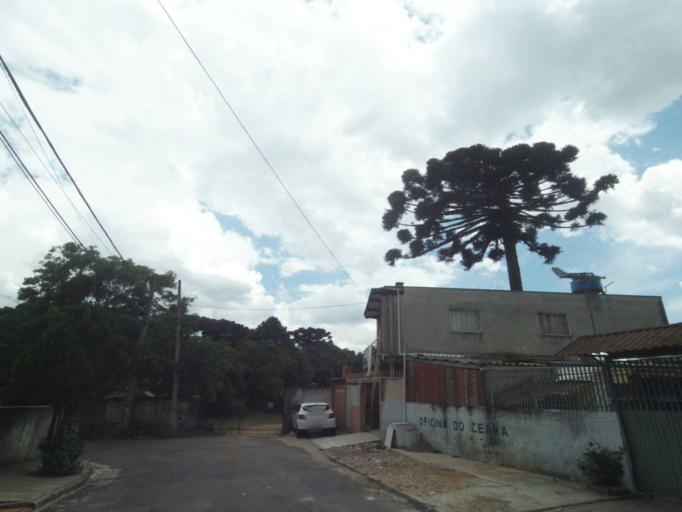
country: BR
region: Parana
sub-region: Curitiba
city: Curitiba
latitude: -25.4577
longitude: -49.3433
